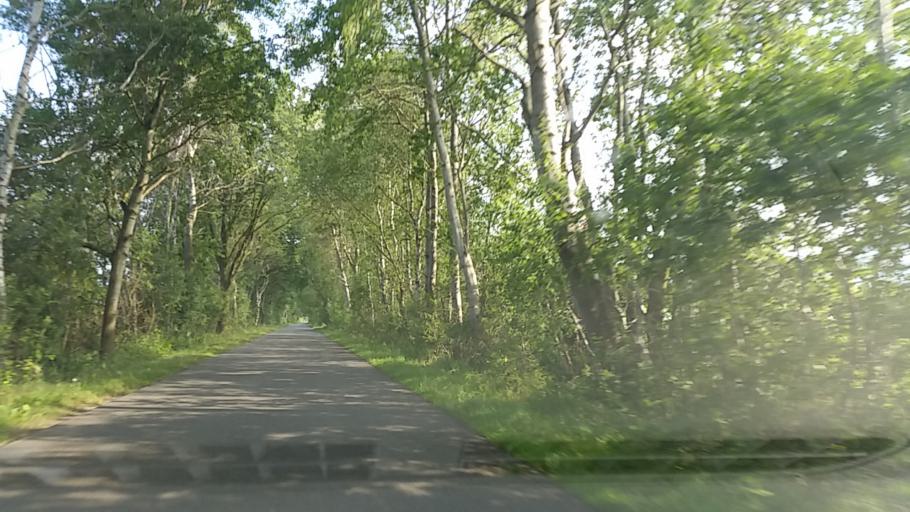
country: DE
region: Lower Saxony
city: Winsen
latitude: 53.3322
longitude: 10.2415
